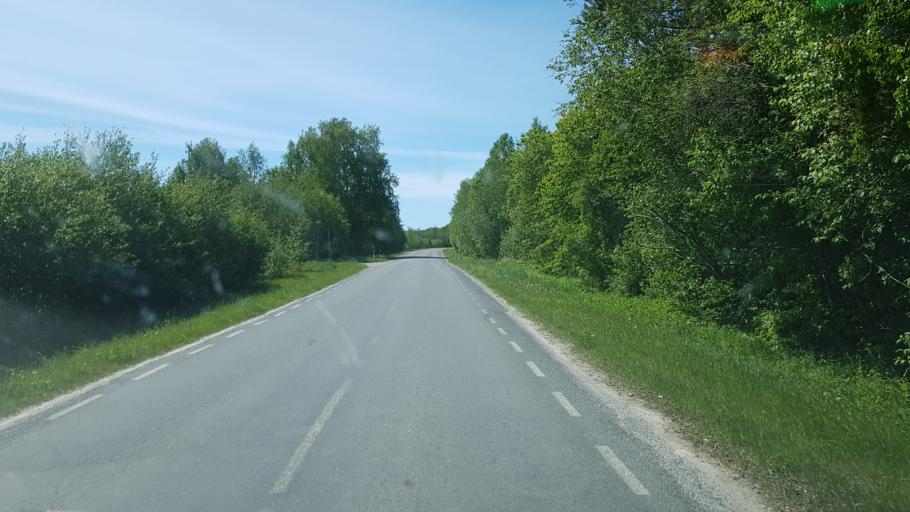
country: EE
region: Saare
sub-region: Kuressaare linn
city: Kuressaare
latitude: 58.2786
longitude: 22.5015
